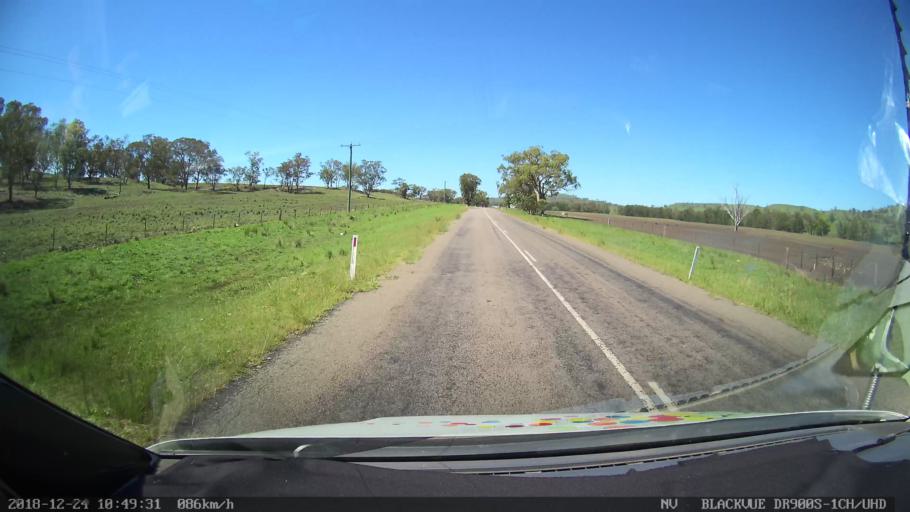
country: AU
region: New South Wales
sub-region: Upper Hunter Shire
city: Merriwa
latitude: -31.9487
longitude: 150.4269
